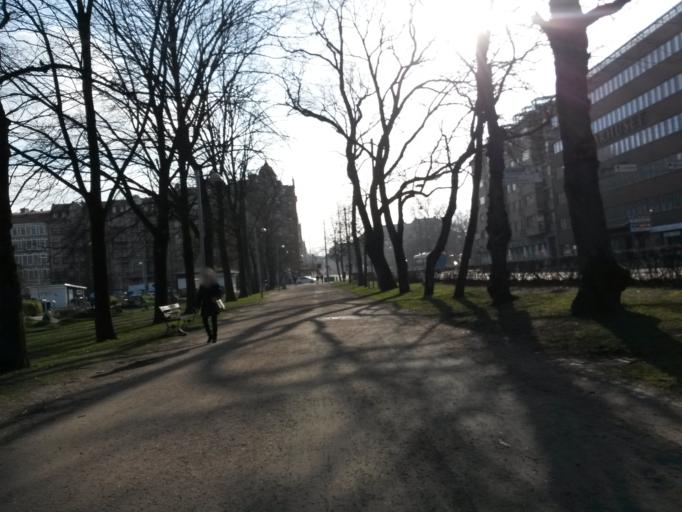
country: SE
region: Vaestra Goetaland
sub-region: Goteborg
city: Goeteborg
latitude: 57.7005
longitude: 11.9783
